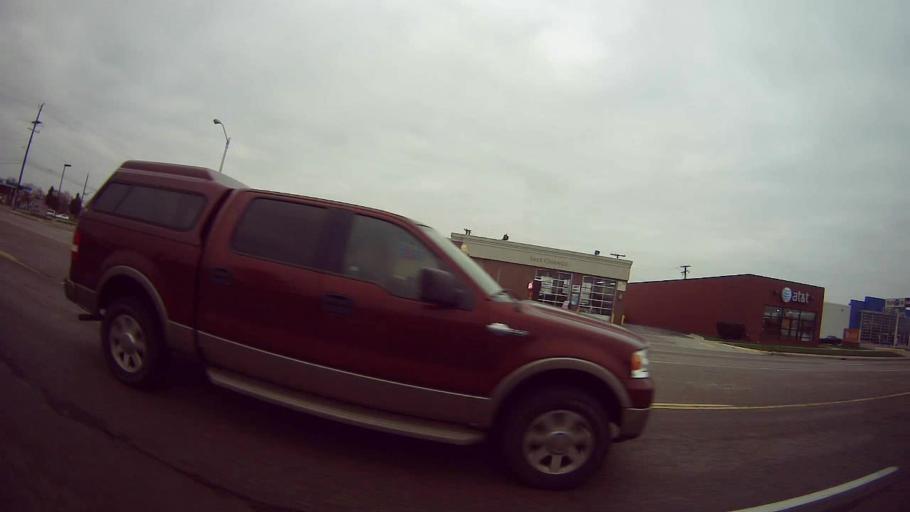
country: US
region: Michigan
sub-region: Oakland County
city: Clawson
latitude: 42.5329
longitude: -83.1071
